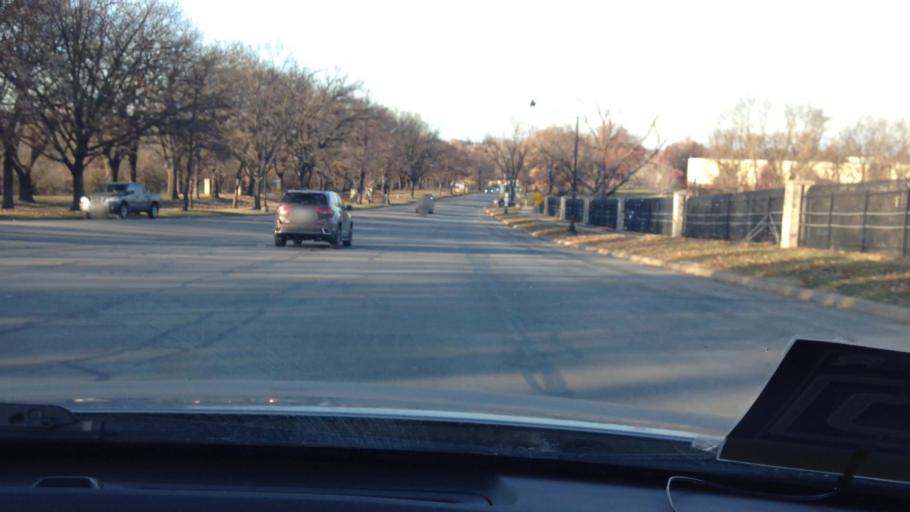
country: US
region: Kansas
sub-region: Leavenworth County
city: Leavenworth
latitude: 39.3311
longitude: -94.9210
